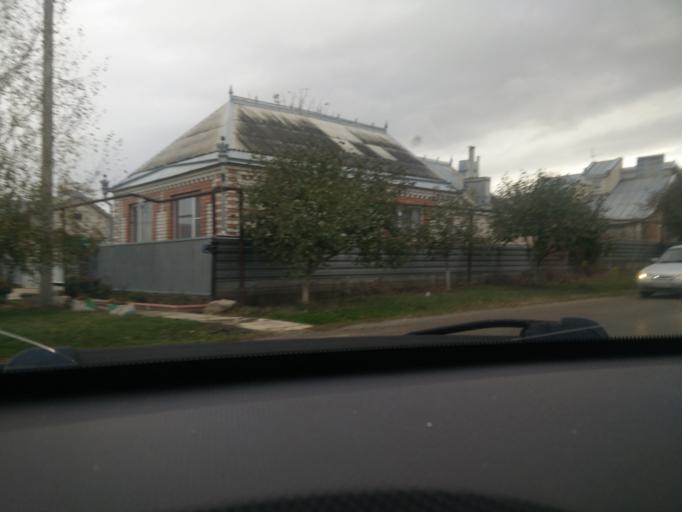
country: RU
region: Stavropol'skiy
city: Ivanovskoye
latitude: 44.5721
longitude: 41.8769
